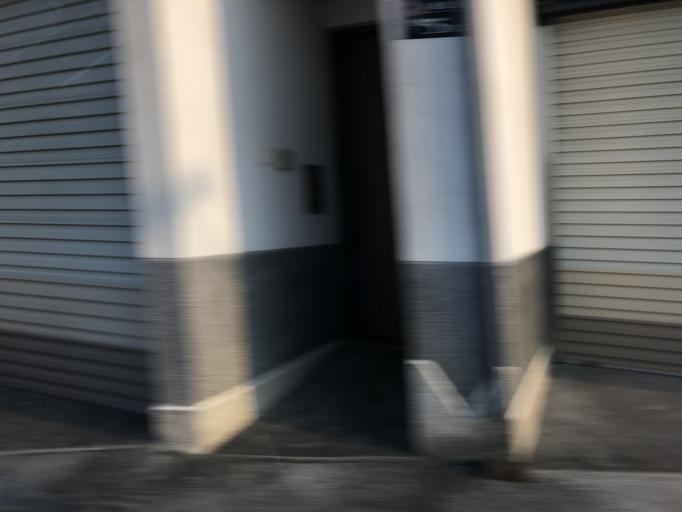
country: TW
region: Taiwan
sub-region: Tainan
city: Tainan
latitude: 23.1361
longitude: 120.2622
